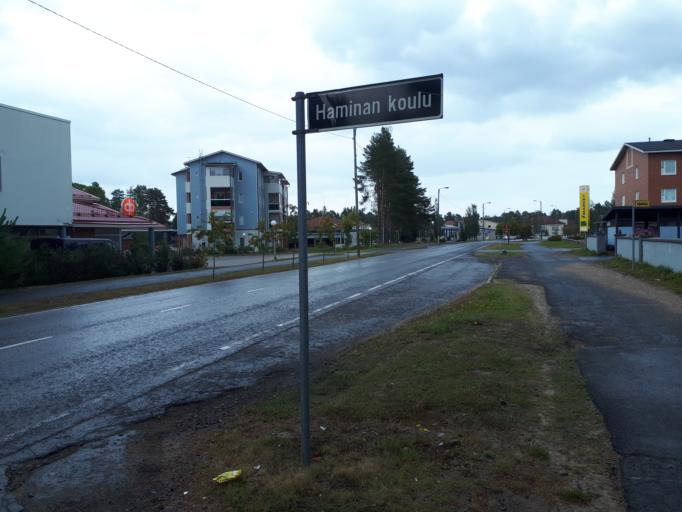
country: FI
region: Northern Ostrobothnia
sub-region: Oulunkaari
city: Ii
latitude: 65.3227
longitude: 25.3734
